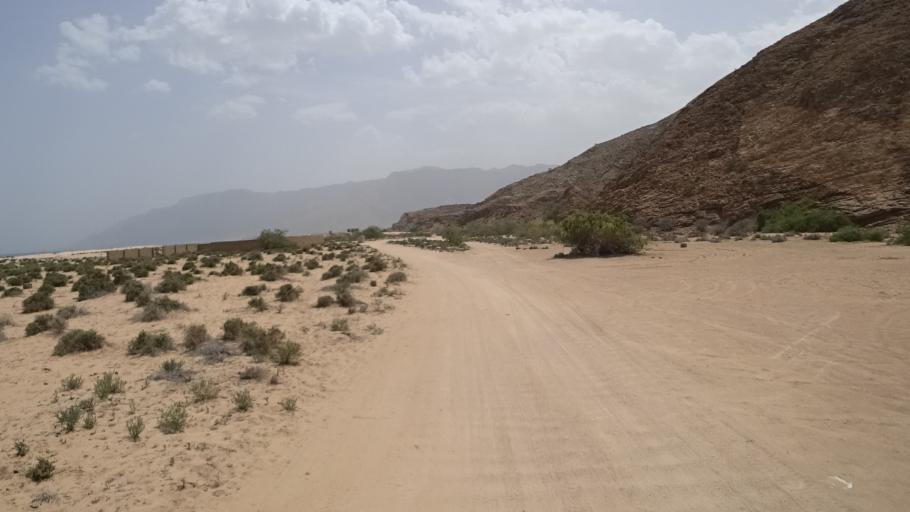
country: OM
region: Muhafazat Masqat
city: Muscat
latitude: 23.4470
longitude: 58.7793
